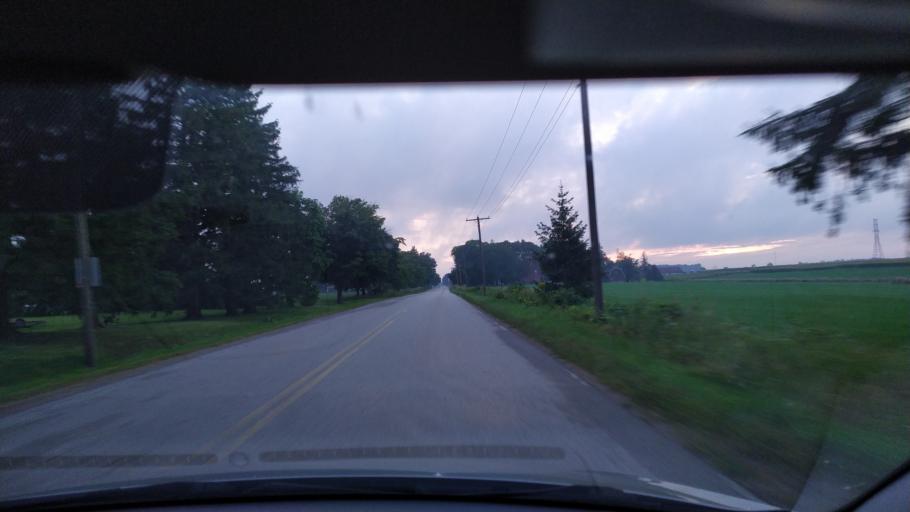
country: CA
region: Ontario
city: Kitchener
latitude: 43.3523
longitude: -80.6843
